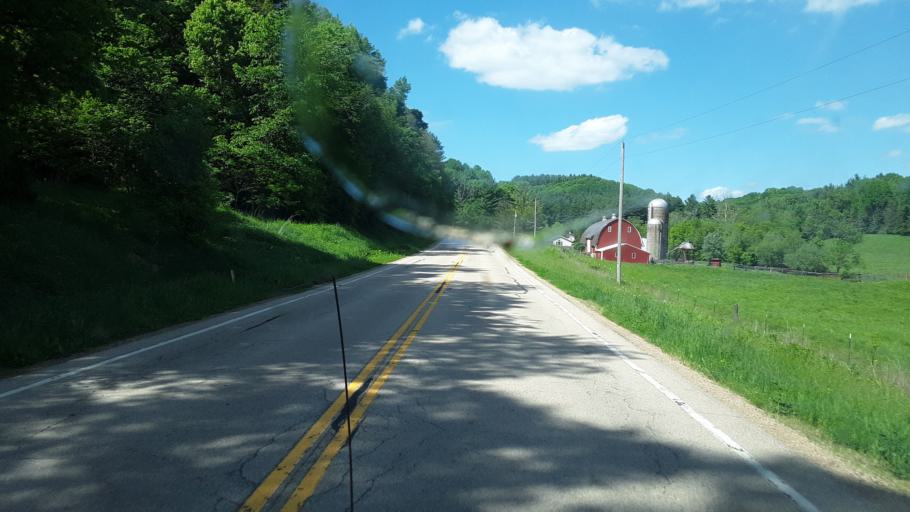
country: US
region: Wisconsin
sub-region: Sauk County
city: Reedsburg
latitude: 43.4682
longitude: -90.2109
